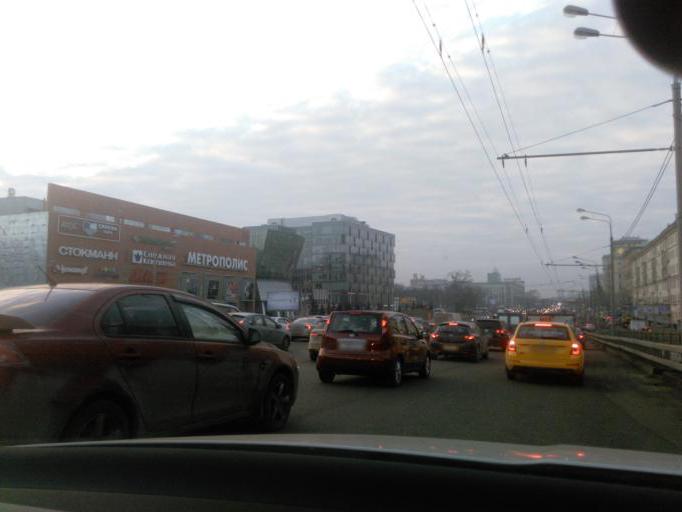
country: RU
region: Moskovskaya
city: Koptevo
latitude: 55.8230
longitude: 37.4944
